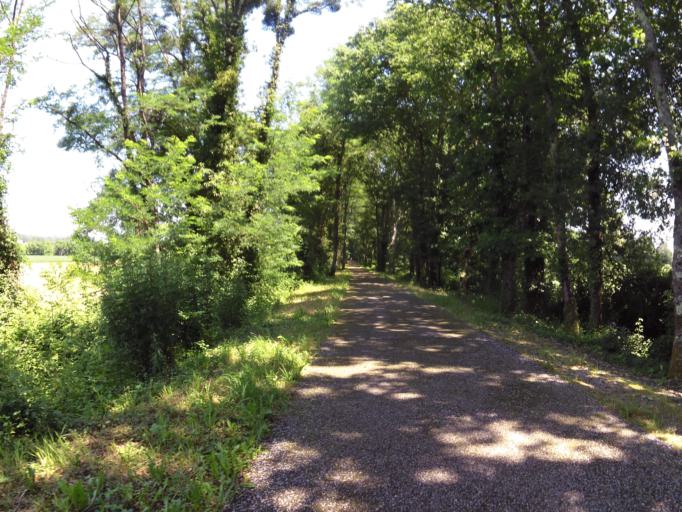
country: FR
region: Aquitaine
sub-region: Departement des Pyrenees-Atlantiques
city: Salies-de-Bearn
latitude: 43.4676
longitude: -0.9427
